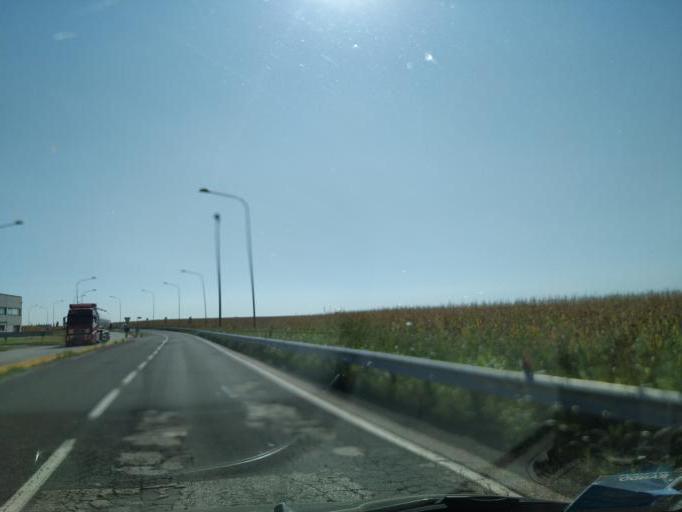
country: IT
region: Emilia-Romagna
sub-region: Provincia di Bologna
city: Decima
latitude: 44.6984
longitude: 11.2305
